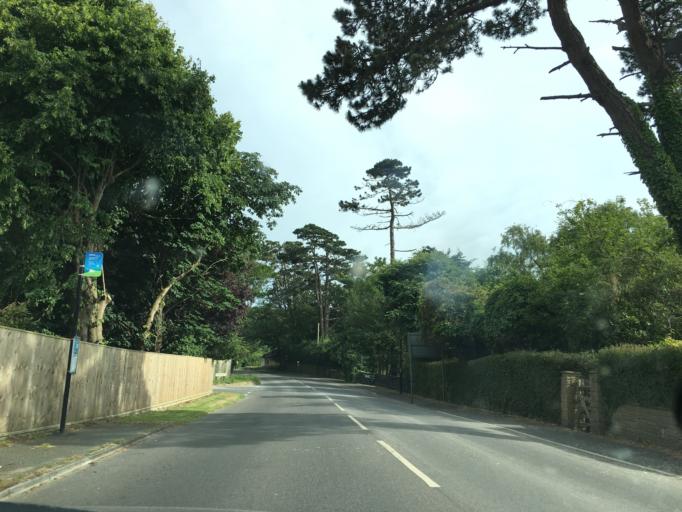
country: GB
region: England
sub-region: Isle of Wight
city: Freshwater
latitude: 50.6754
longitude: -1.5088
